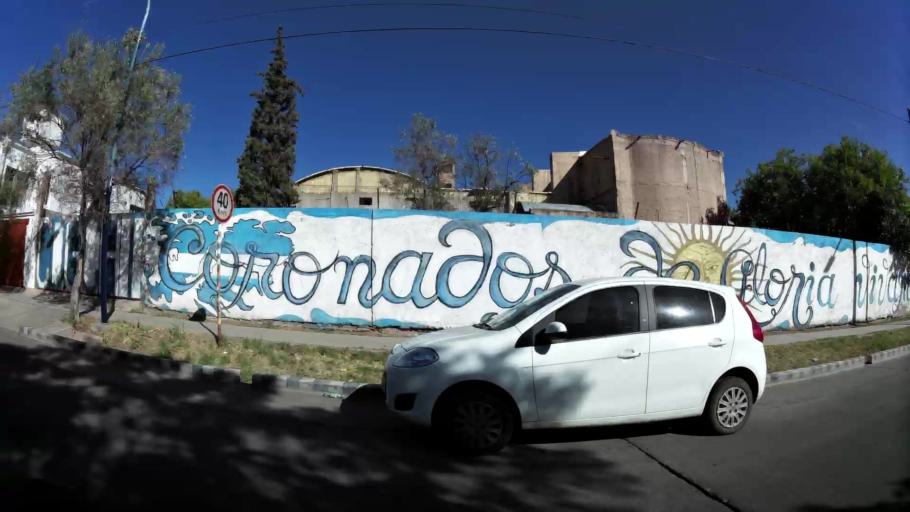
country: AR
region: Mendoza
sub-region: Departamento de Godoy Cruz
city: Godoy Cruz
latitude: -32.9217
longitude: -68.8418
